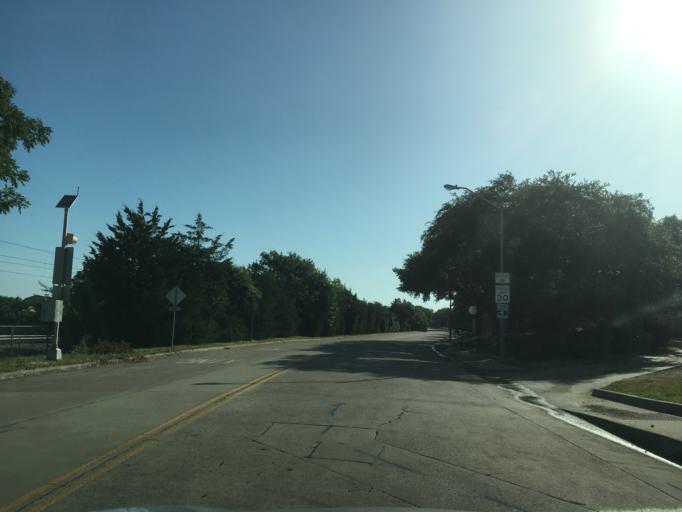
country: US
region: Texas
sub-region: Dallas County
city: Richardson
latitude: 32.8892
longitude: -96.7292
